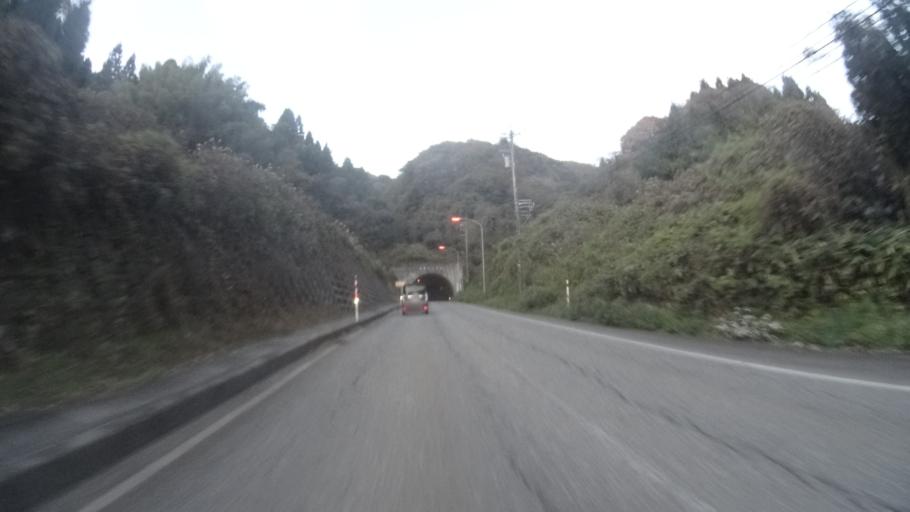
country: JP
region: Ishikawa
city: Nanao
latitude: 37.3257
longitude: 136.8191
